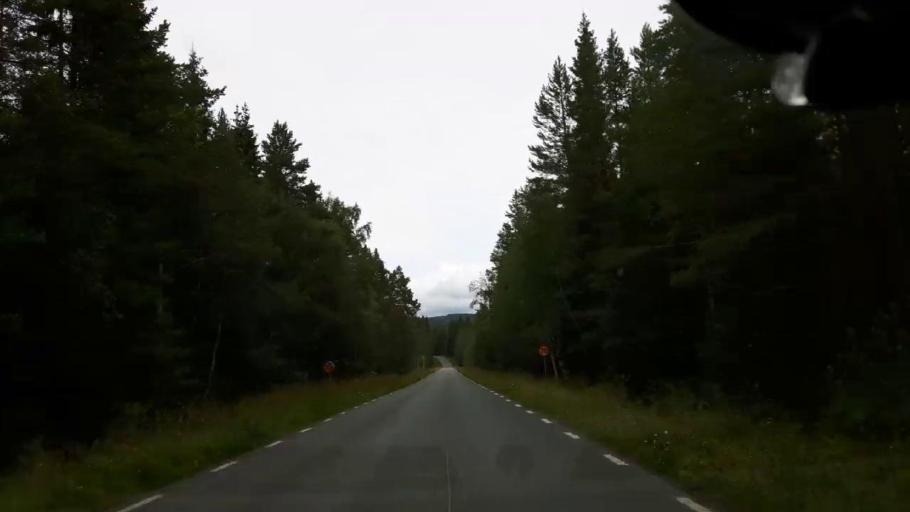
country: SE
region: Jaemtland
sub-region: Krokoms Kommun
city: Valla
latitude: 63.4622
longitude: 14.0629
